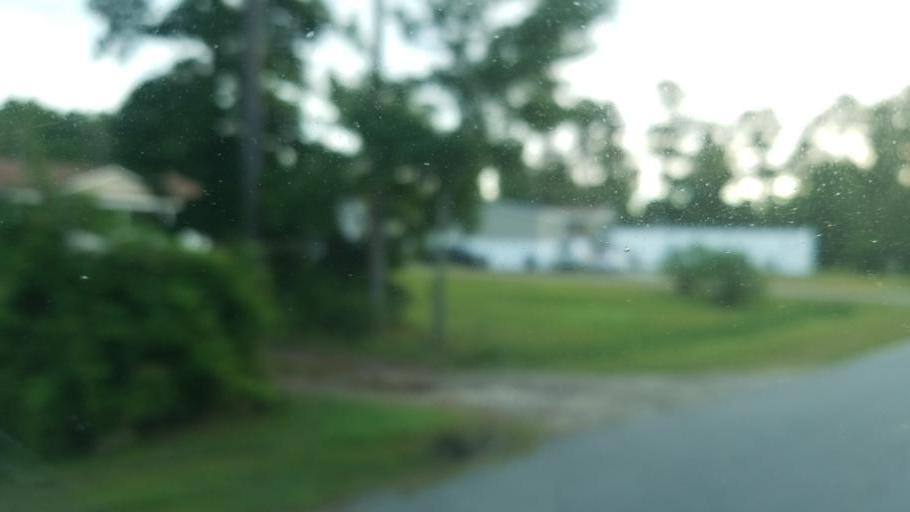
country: US
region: North Carolina
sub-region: Dare County
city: Wanchese
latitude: 35.8404
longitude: -75.6337
